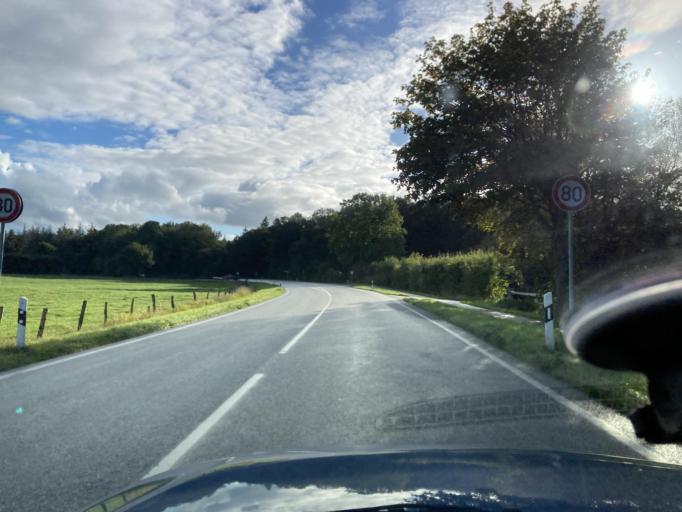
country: DE
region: Schleswig-Holstein
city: Fockbek
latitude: 54.2813
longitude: 9.5744
